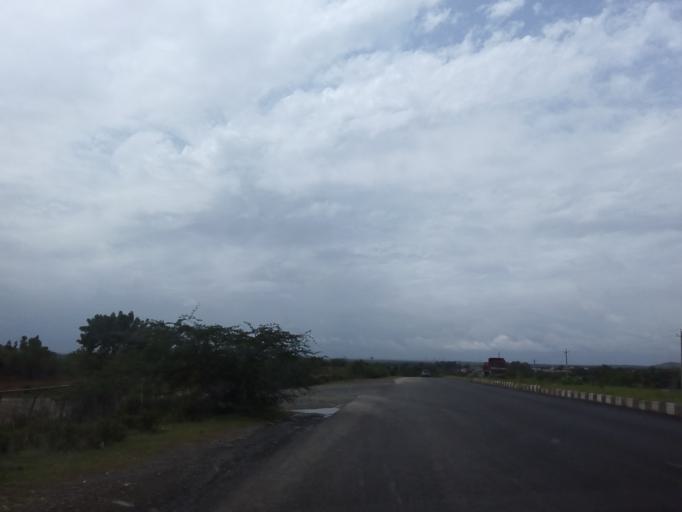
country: IN
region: Karnataka
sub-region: Haveri
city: Byadgi
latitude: 14.7025
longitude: 75.5212
